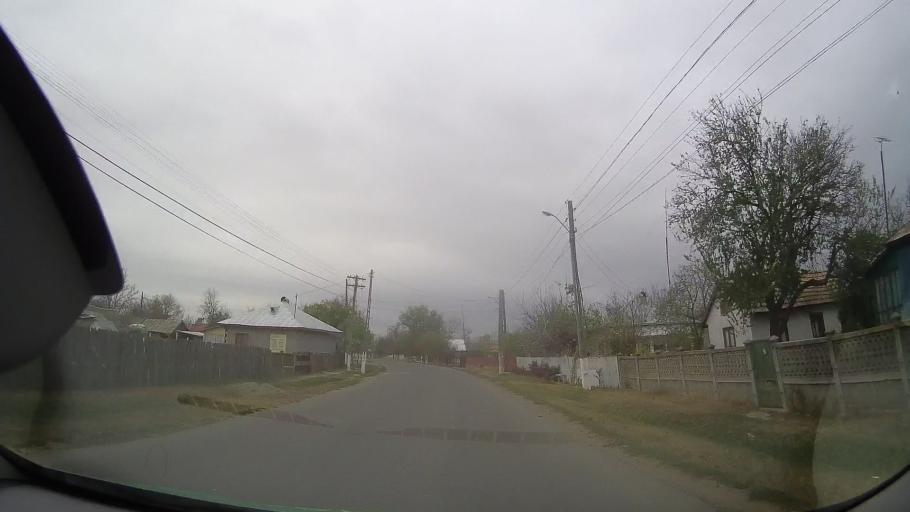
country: RO
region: Braila
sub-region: Comuna Ulmu
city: Jugureanu
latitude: 44.9434
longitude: 27.2756
